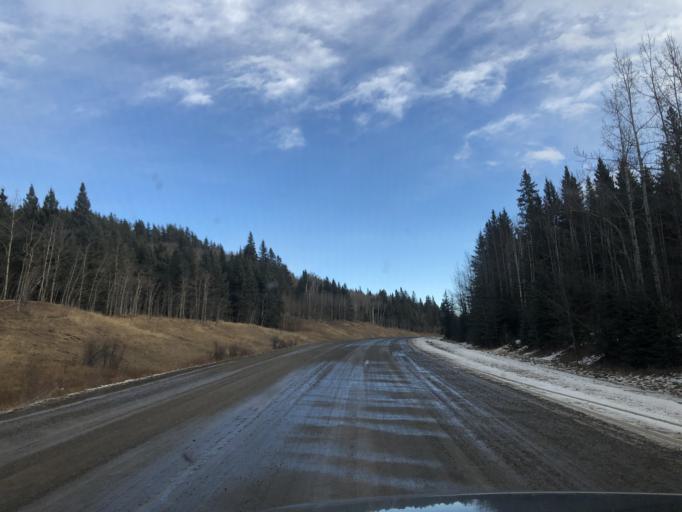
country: CA
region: Alberta
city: Cochrane
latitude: 51.0433
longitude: -114.7546
